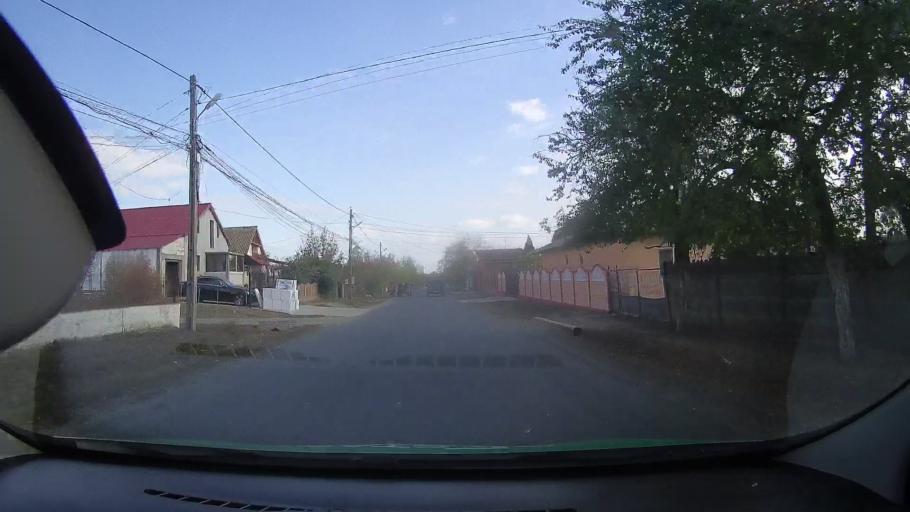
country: RO
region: Constanta
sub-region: Comuna Sacele
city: Sacele
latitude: 44.4883
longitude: 28.6398
